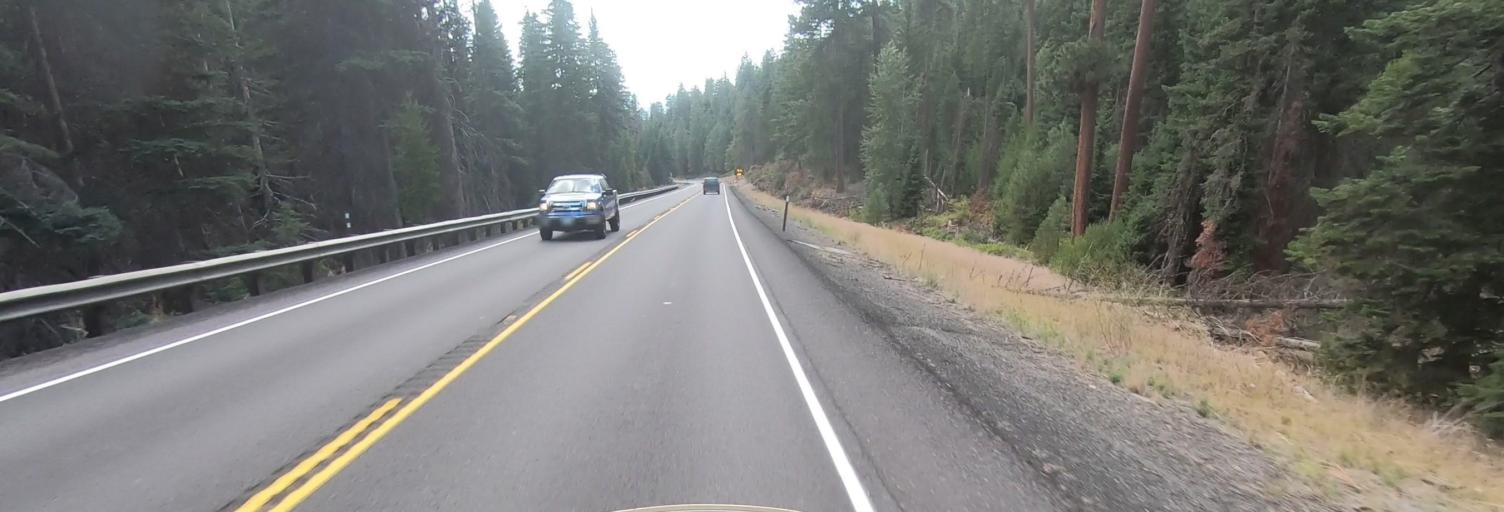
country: US
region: Washington
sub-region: Chelan County
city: Cashmere
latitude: 47.3337
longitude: -120.6346
